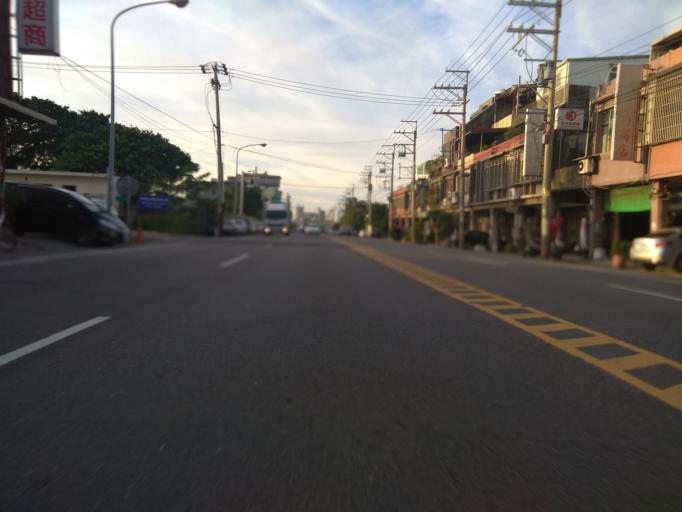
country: TW
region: Taiwan
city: Taoyuan City
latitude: 24.9800
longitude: 121.1931
